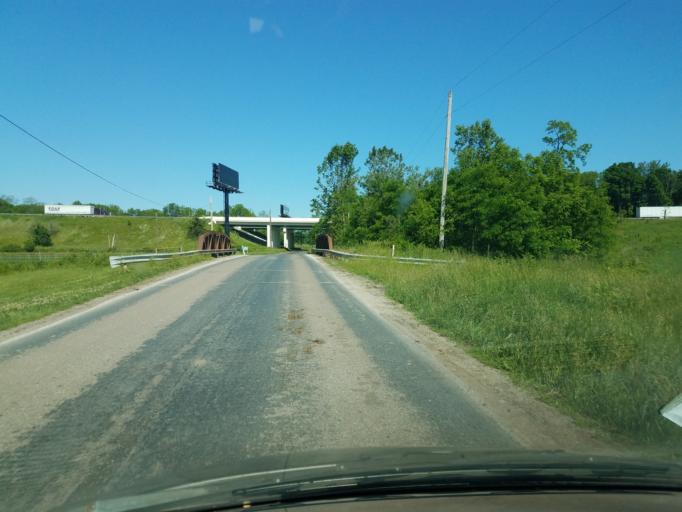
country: US
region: Ohio
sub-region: Knox County
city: Fredericktown
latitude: 40.5459
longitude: -82.6538
